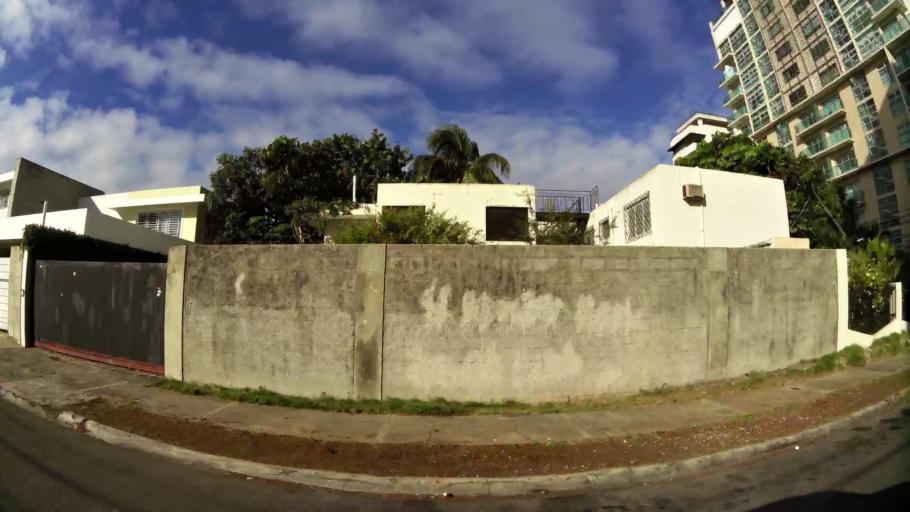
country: DO
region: Nacional
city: La Julia
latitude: 18.4725
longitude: -69.9367
